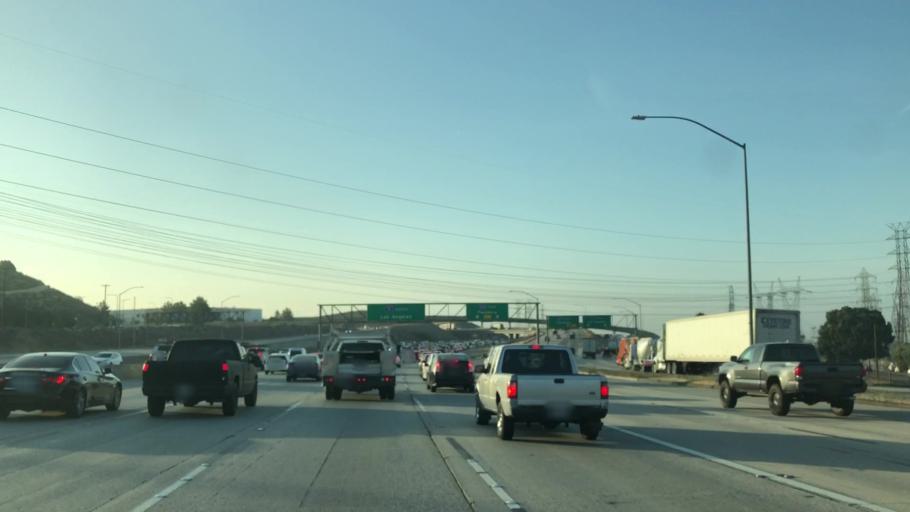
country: US
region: California
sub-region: Los Angeles County
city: San Fernando
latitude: 34.3240
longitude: -118.4951
